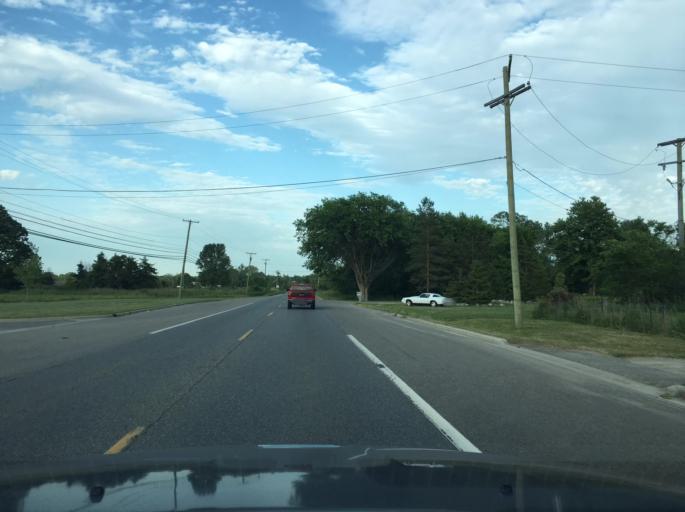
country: US
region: Michigan
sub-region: Macomb County
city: New Haven
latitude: 42.7175
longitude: -82.8887
